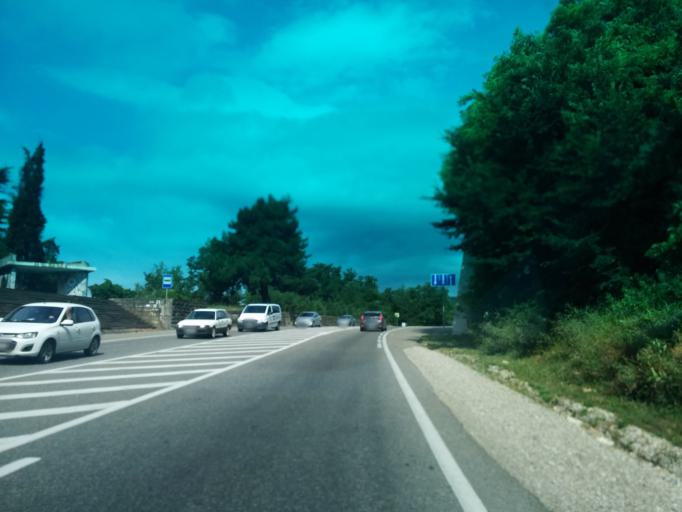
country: RU
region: Krasnodarskiy
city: Nebug
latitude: 44.1667
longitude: 38.9906
